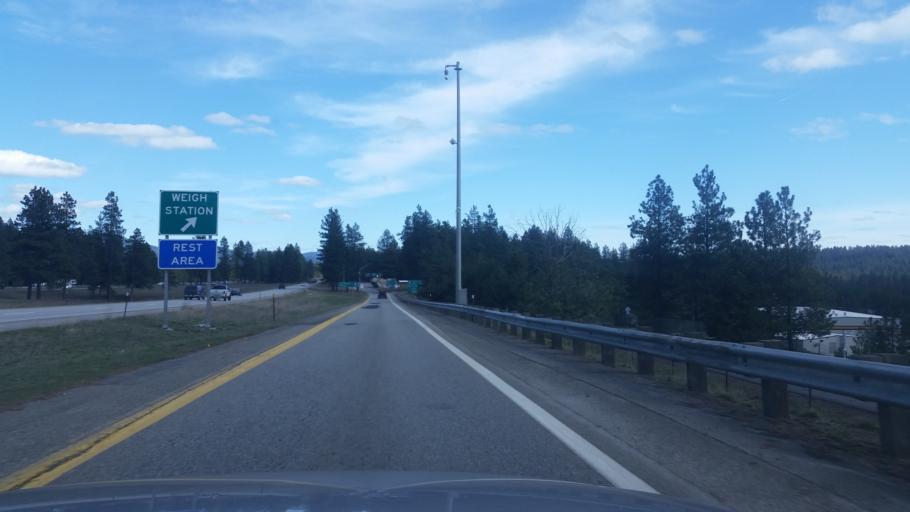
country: US
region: Idaho
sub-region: Kootenai County
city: Post Falls
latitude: 47.7085
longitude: -116.8720
